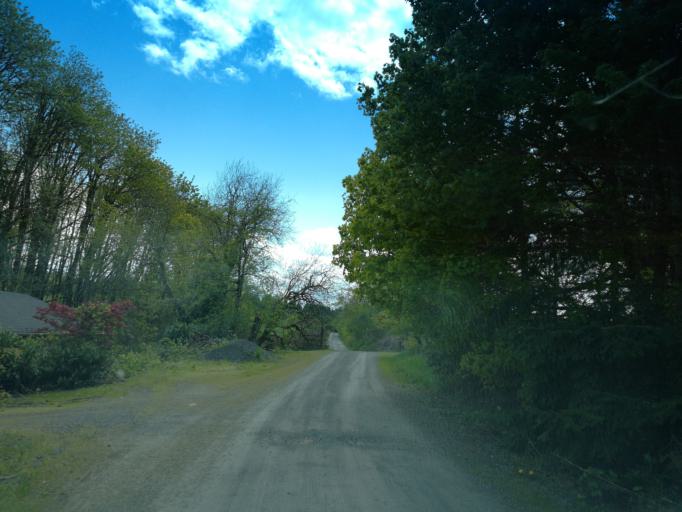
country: US
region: Oregon
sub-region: Clackamas County
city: Damascus
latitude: 45.4542
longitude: -122.4473
